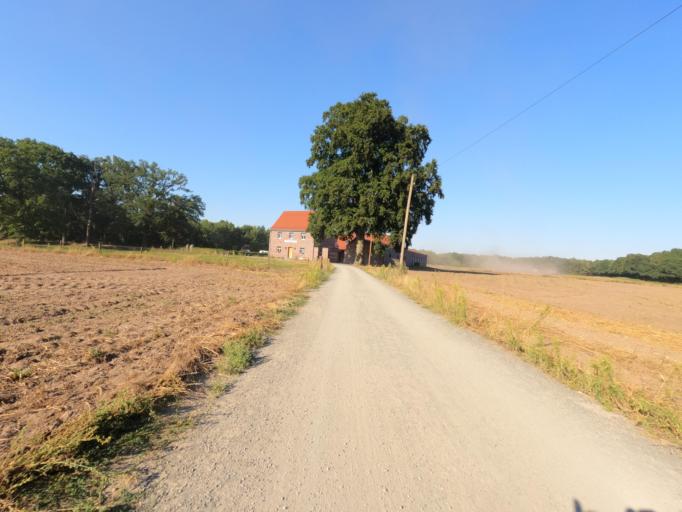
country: NL
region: Limburg
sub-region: Gemeente Roerdalen
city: Vlodrop
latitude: 51.1361
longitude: 6.1094
